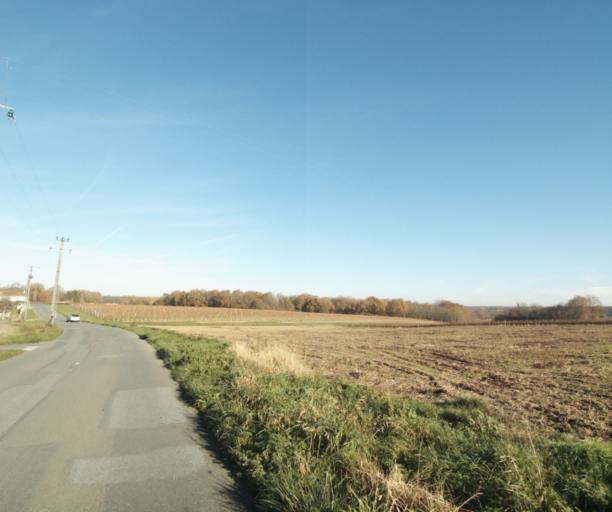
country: FR
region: Poitou-Charentes
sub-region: Departement de la Charente-Maritime
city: Chaniers
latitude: 45.7380
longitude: -0.5573
